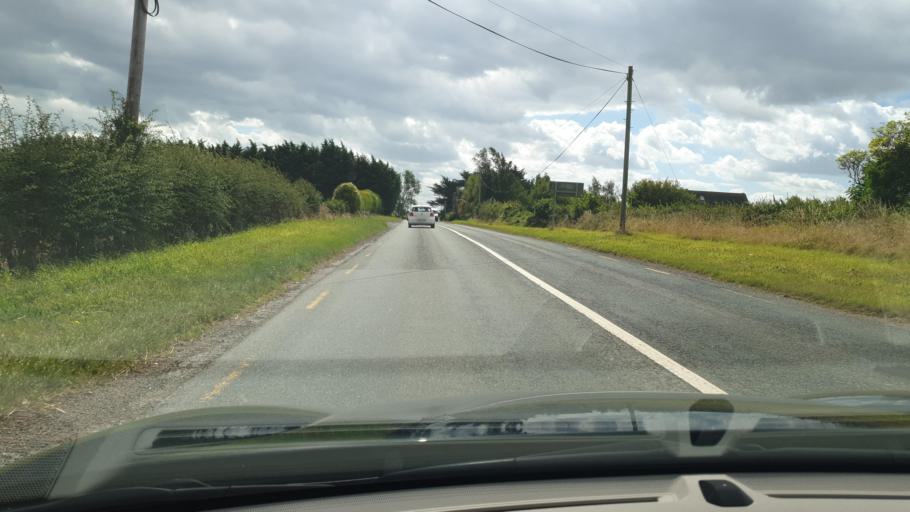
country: IE
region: Leinster
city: Lusk
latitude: 53.5537
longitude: -6.1534
